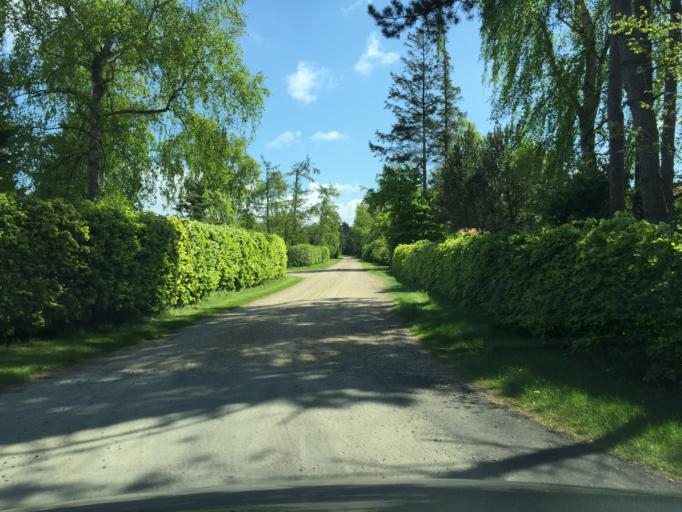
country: DK
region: Zealand
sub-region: Vordingborg Kommune
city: Stege
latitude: 55.0307
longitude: 12.2957
